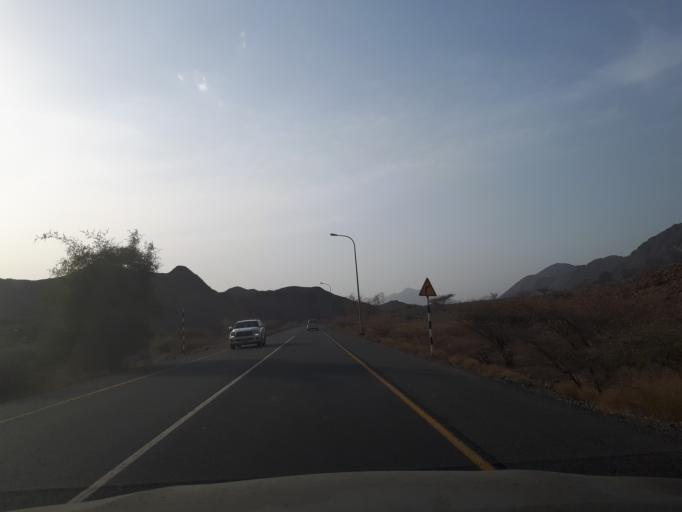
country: OM
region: Muhafazat ad Dakhiliyah
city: Sufalat Sama'il
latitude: 23.1621
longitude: 58.1048
